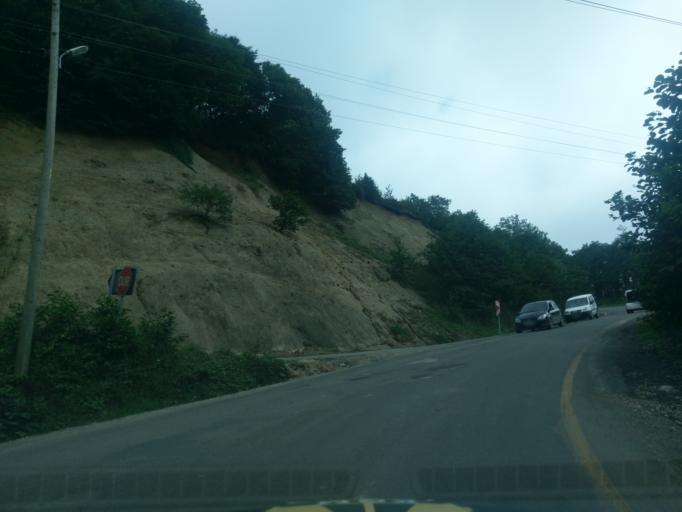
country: TR
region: Ordu
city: Gurgentepe
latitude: 40.8495
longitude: 37.6539
